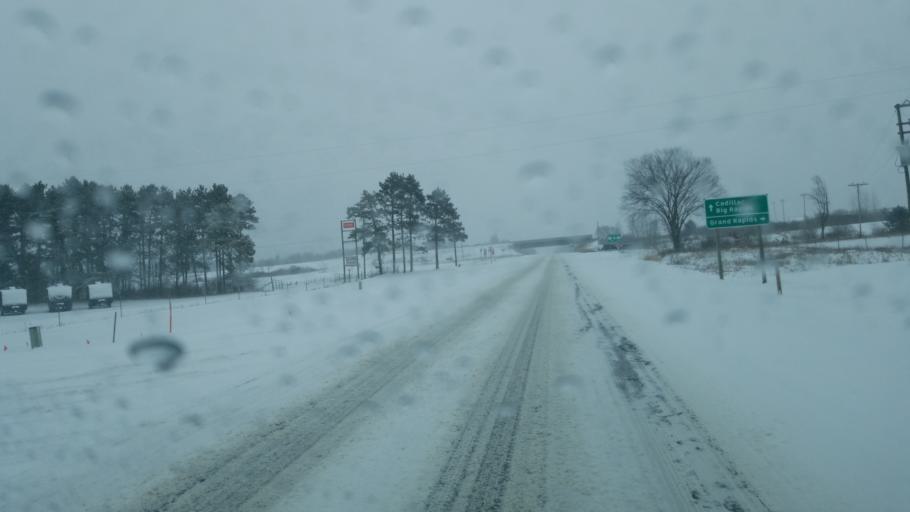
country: US
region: Michigan
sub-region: Mecosta County
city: Big Rapids
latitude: 43.5837
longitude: -85.4944
